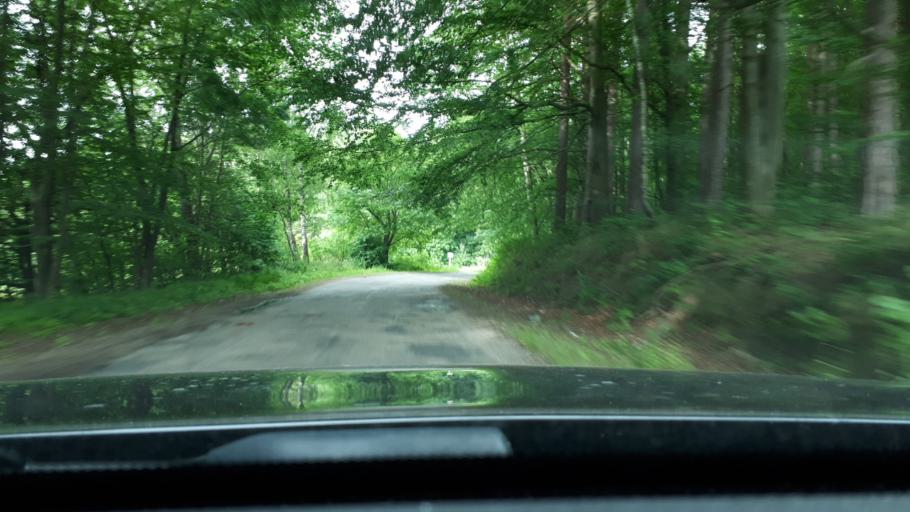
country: PL
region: Warmian-Masurian Voivodeship
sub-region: Powiat ostrodzki
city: Gierzwald
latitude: 53.6384
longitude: 20.0867
